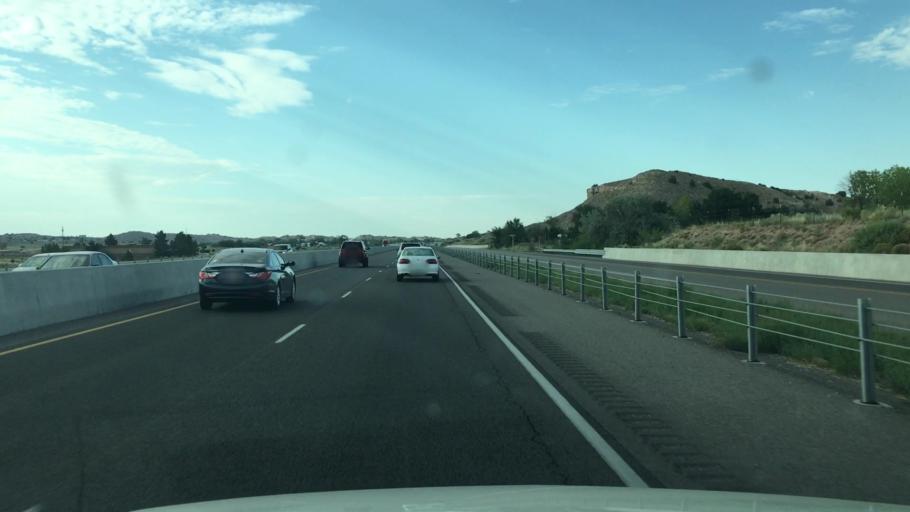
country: US
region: New Mexico
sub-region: Santa Fe County
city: El Valle de Arroyo Seco
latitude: 35.9496
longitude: -106.0209
